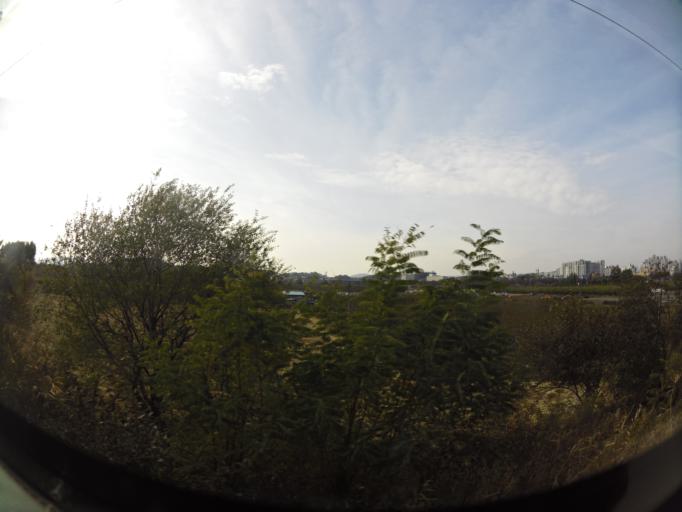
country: KR
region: Daejeon
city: Songgang-dong
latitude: 36.5876
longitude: 127.3062
